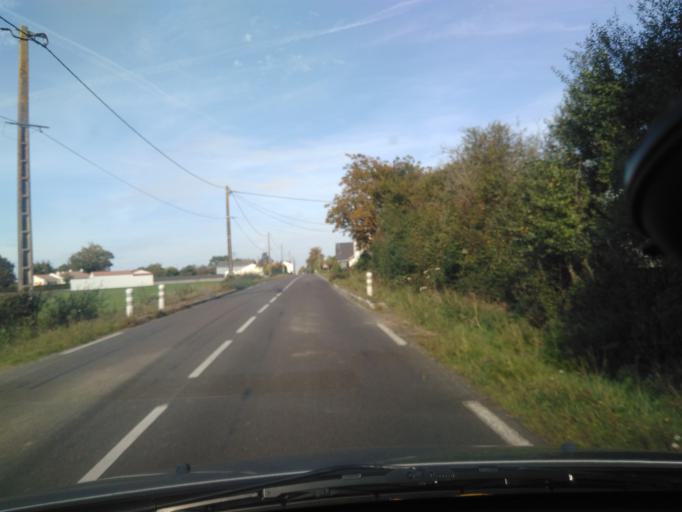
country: FR
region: Pays de la Loire
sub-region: Departement de la Vendee
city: Nieul-le-Dolent
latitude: 46.5447
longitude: -1.5325
